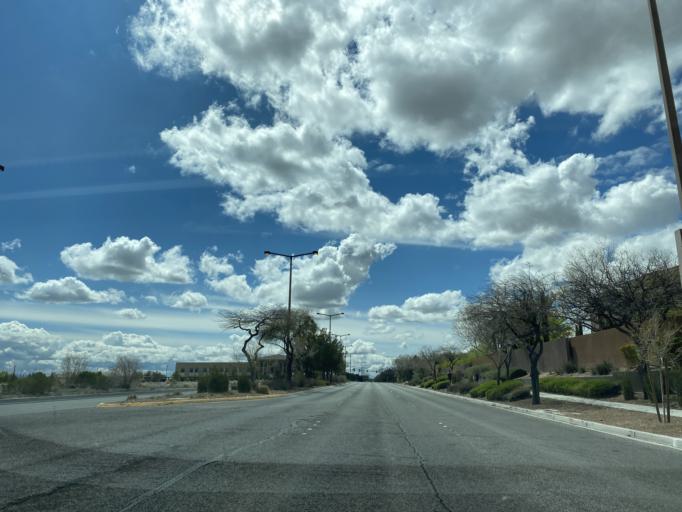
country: US
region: Nevada
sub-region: Clark County
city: Summerlin South
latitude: 36.1708
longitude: -115.3157
